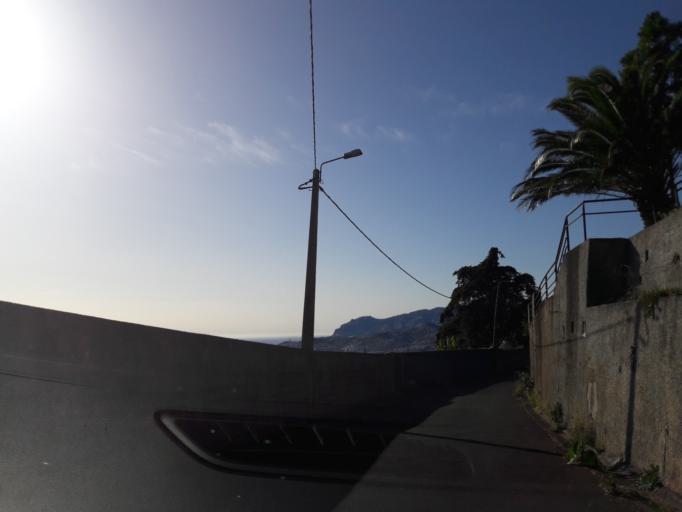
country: PT
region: Madeira
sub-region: Funchal
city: Nossa Senhora do Monte
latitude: 32.6543
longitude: -16.8755
